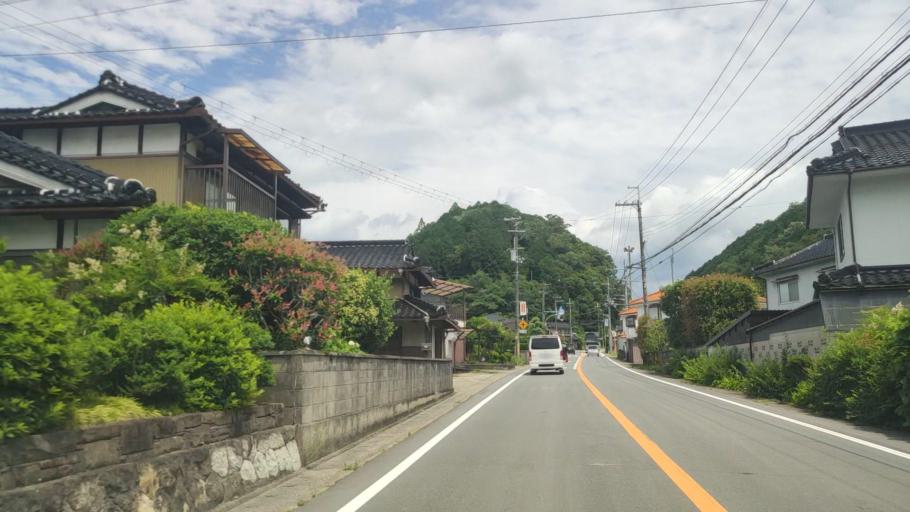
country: JP
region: Hyogo
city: Yamazakicho-nakabirose
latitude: 34.9933
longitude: 134.3976
